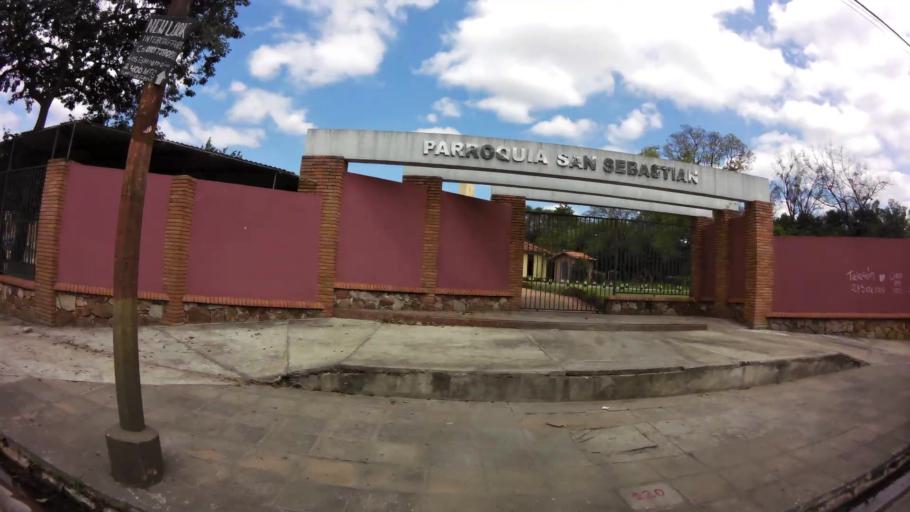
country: PY
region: Central
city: Fernando de la Mora
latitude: -25.3062
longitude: -57.5452
